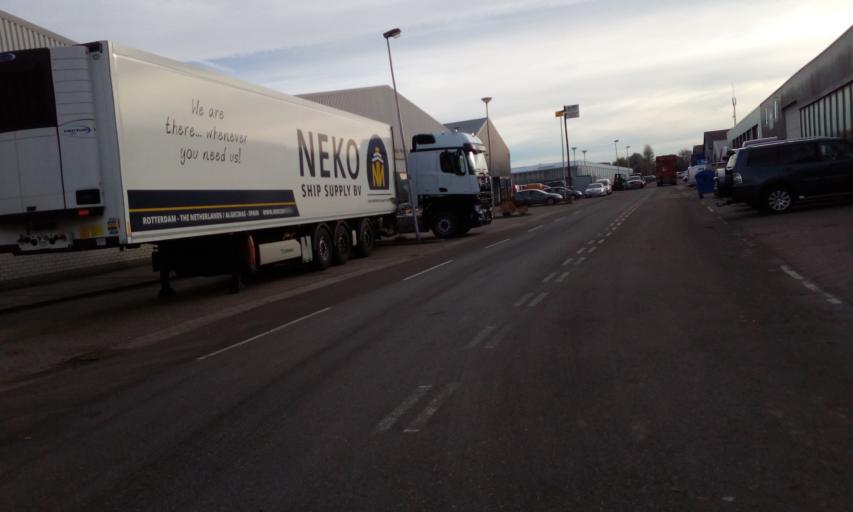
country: NL
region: South Holland
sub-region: Gemeente Lansingerland
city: Bergschenhoek
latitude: 51.9958
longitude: 4.5159
